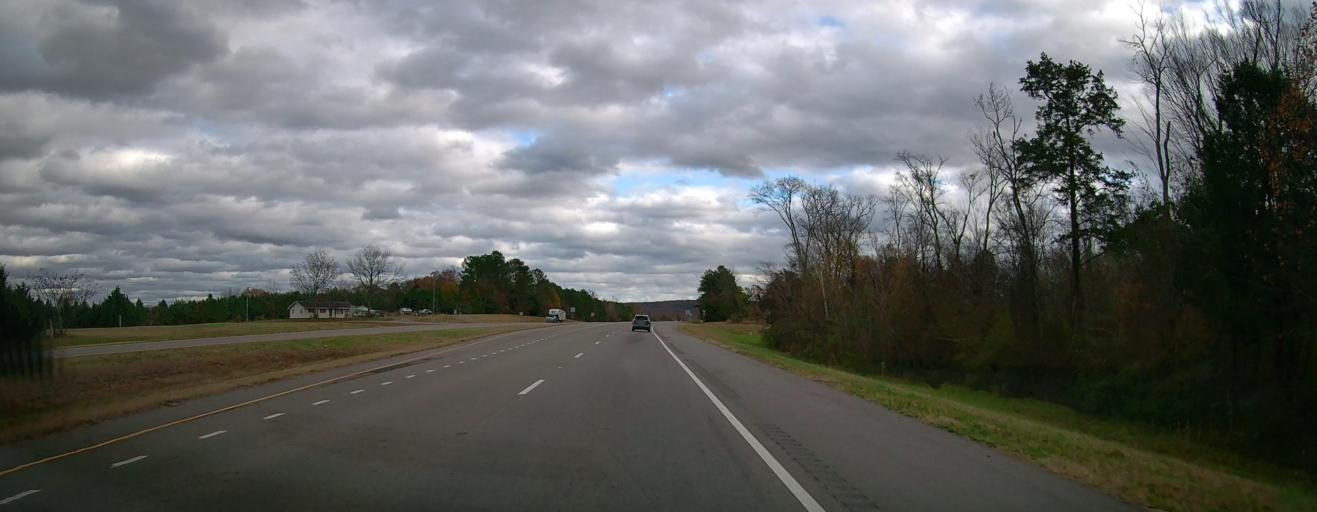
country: US
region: Alabama
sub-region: Morgan County
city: Danville
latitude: 34.3421
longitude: -87.0291
